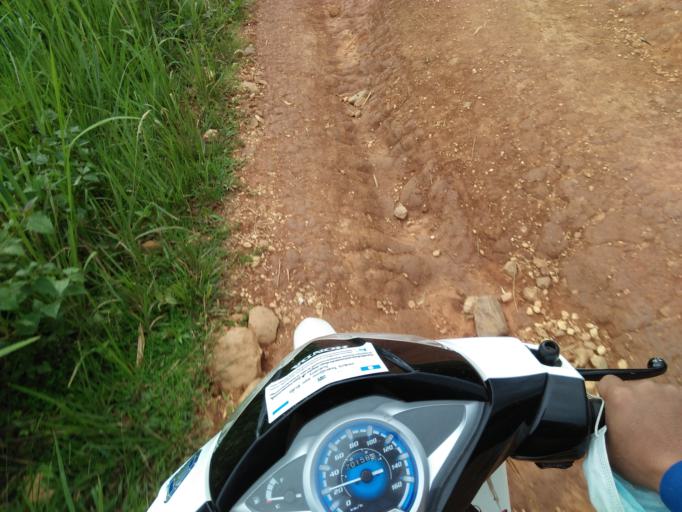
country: TH
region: Chiang Rai
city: Wiang Kaen
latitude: 19.8100
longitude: 100.7292
